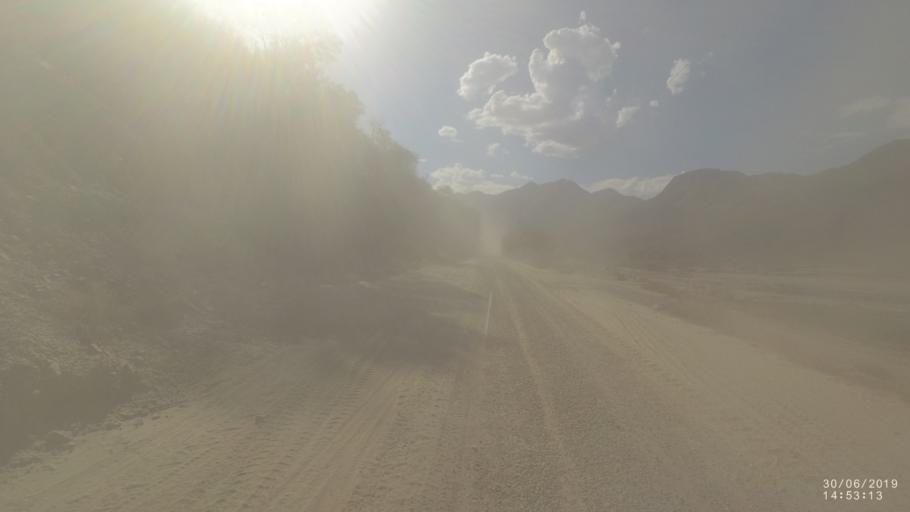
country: BO
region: Cochabamba
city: Irpa Irpa
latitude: -17.7652
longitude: -66.3480
